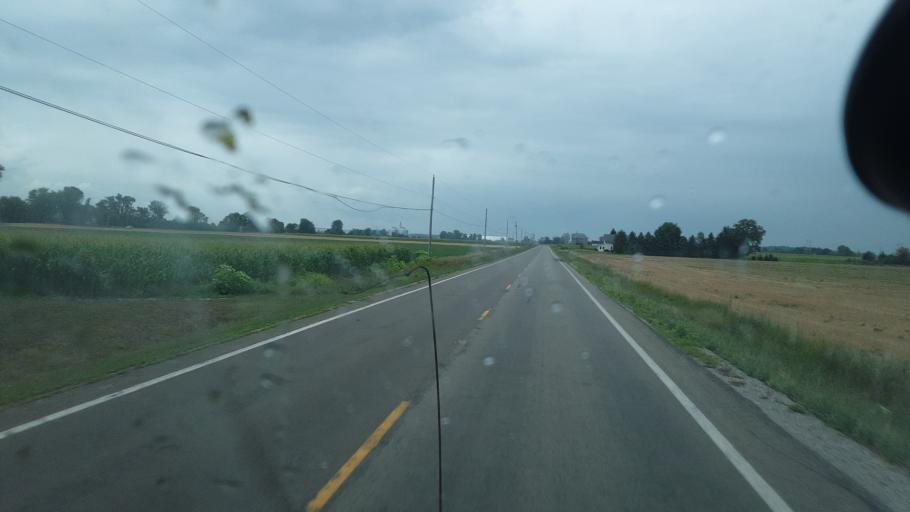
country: US
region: Ohio
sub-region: Defiance County
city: Hicksville
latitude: 41.2961
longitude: -84.7170
